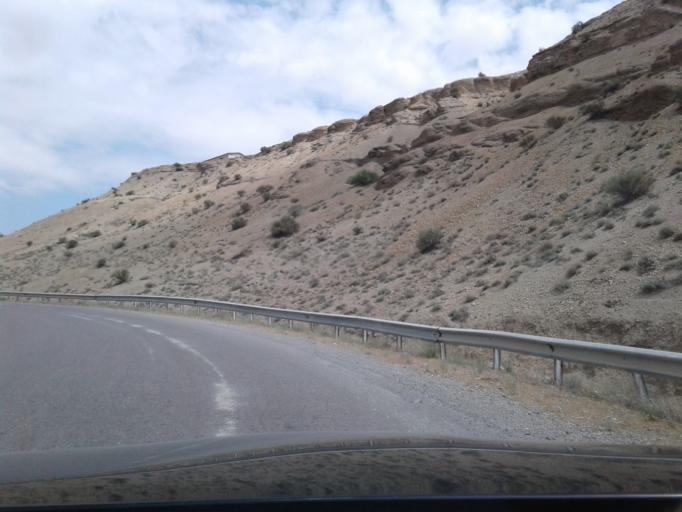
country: TM
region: Ahal
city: Baharly
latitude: 38.5037
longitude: 57.0811
